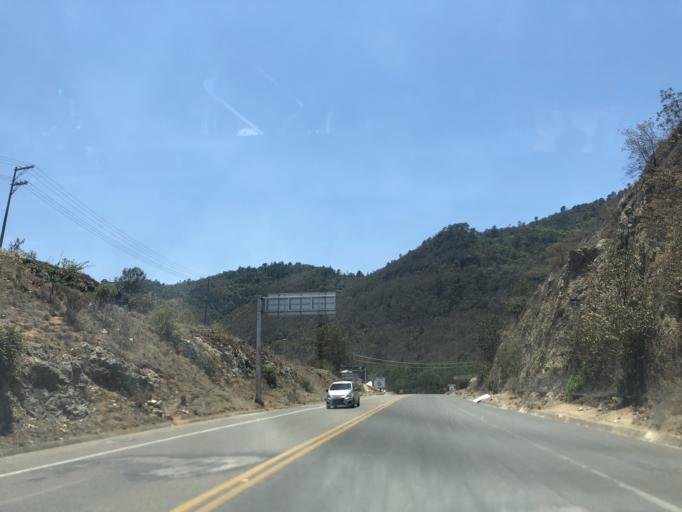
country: MX
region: Chiapas
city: San Cristobal de las Casas
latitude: 16.7205
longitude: -92.6548
